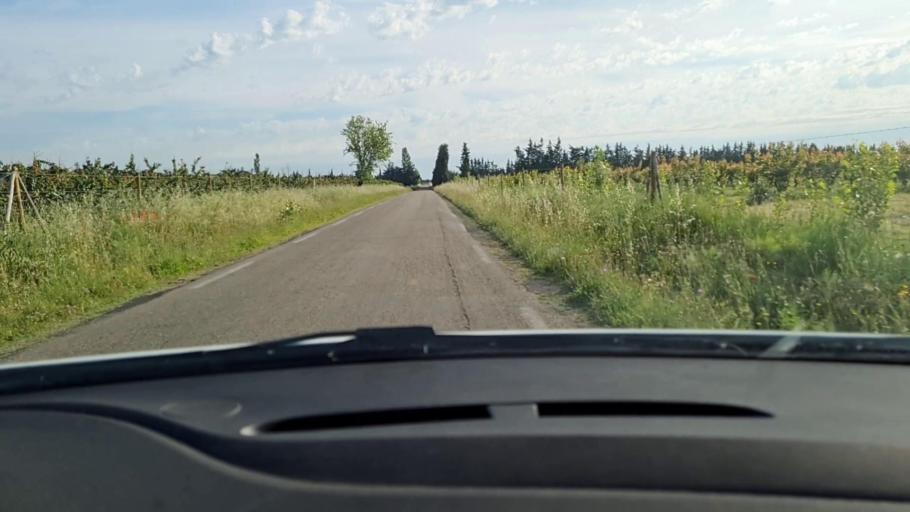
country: FR
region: Languedoc-Roussillon
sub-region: Departement du Gard
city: Jonquieres-Saint-Vincent
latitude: 43.8063
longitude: 4.5422
